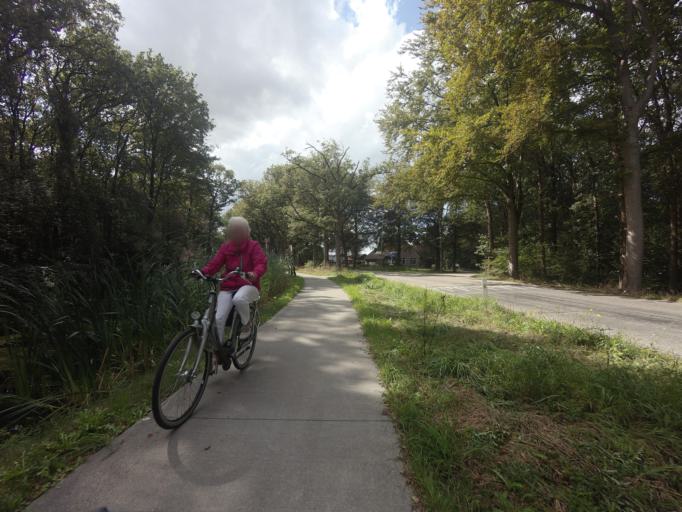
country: NL
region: Drenthe
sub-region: Gemeente Westerveld
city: Dwingeloo
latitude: 52.9540
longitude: 6.3084
